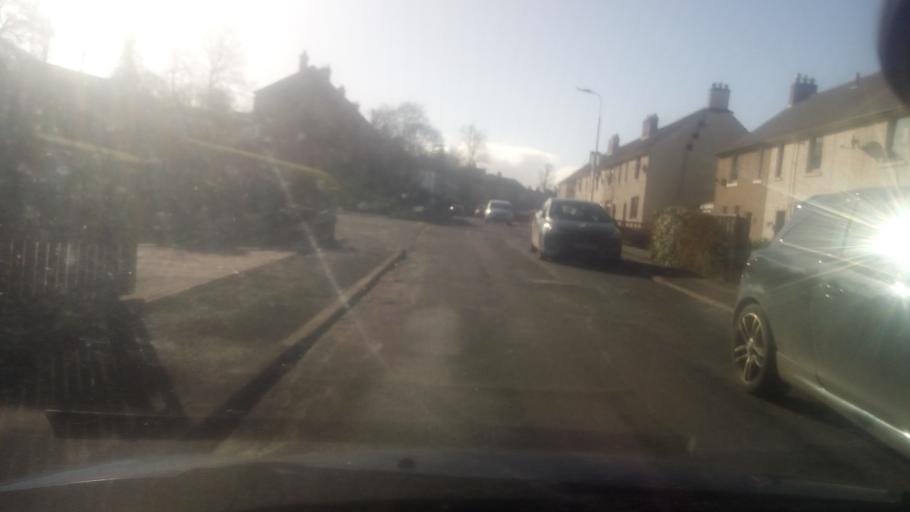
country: GB
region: Scotland
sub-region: The Scottish Borders
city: Jedburgh
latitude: 55.4805
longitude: -2.5466
